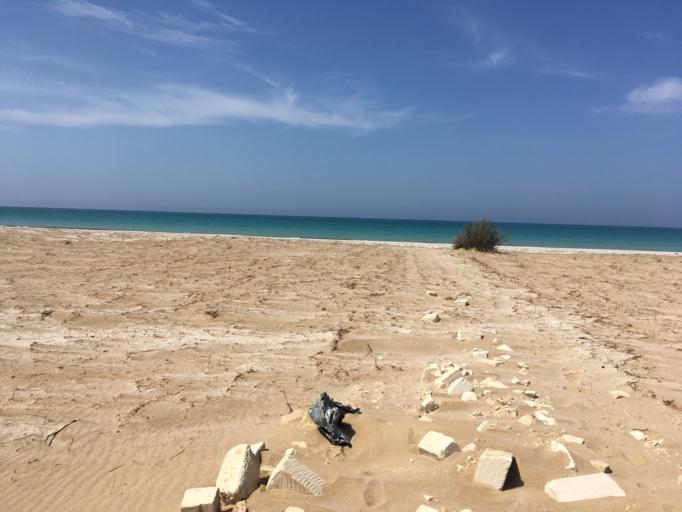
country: KZ
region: Mangghystau
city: Omirzaq
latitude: 43.4345
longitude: 51.3170
